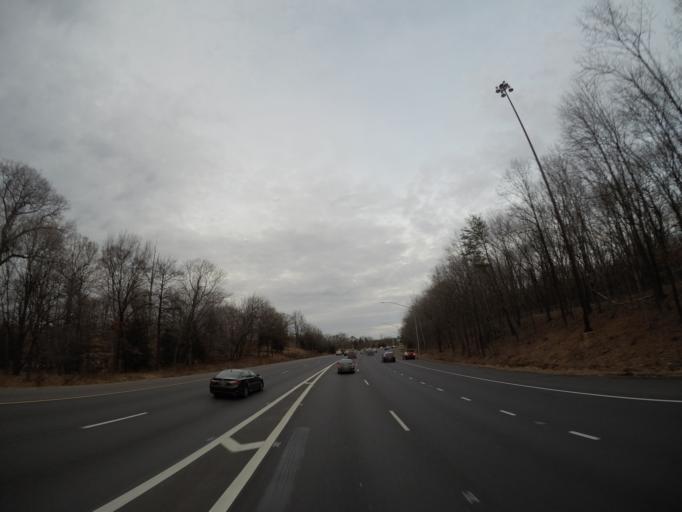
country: US
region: Maryland
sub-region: Montgomery County
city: Hillandale
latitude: 39.0294
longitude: -76.9477
